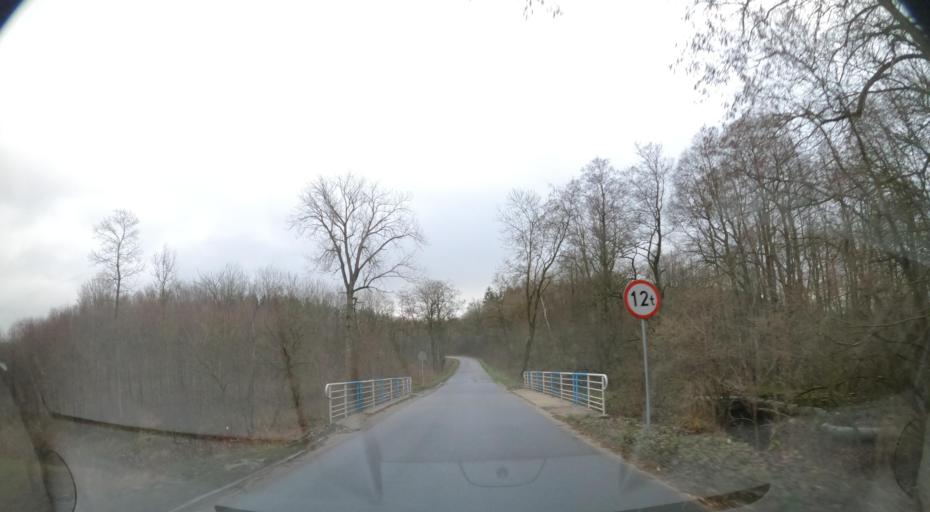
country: PL
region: Greater Poland Voivodeship
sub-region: Powiat pilski
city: Lobzenica
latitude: 53.2347
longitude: 17.3092
